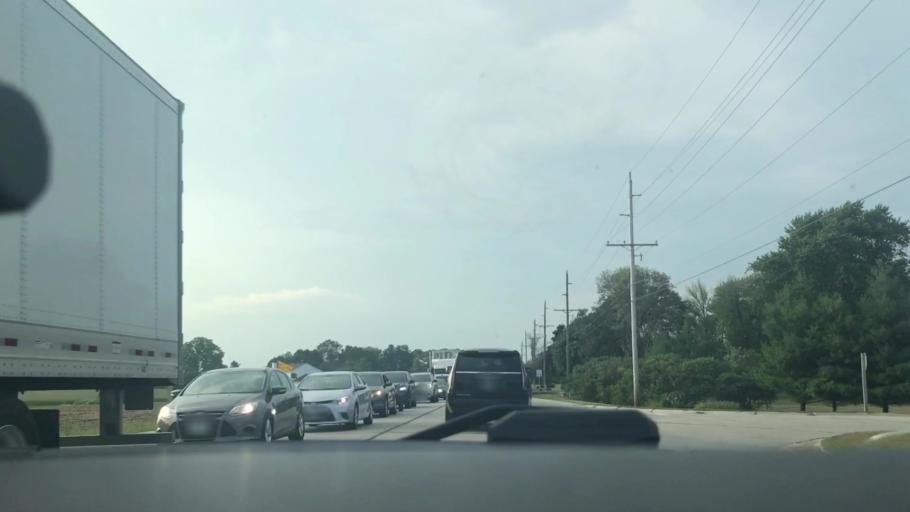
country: US
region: Wisconsin
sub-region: Washington County
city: Slinger
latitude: 43.3745
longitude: -88.3380
